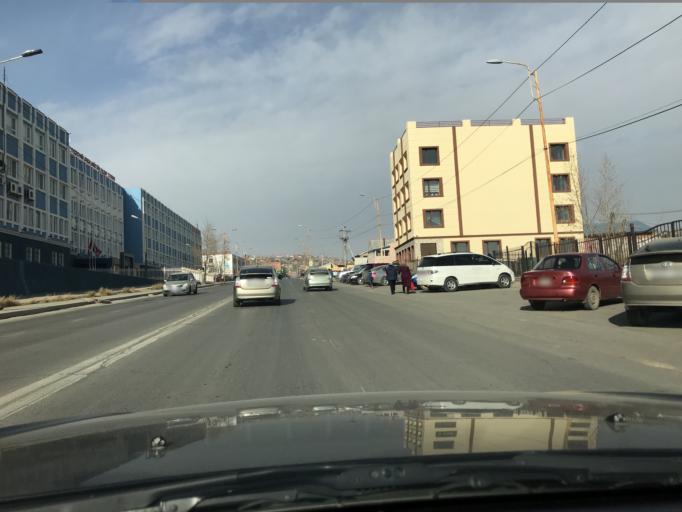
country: MN
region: Ulaanbaatar
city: Ulaanbaatar
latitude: 47.9289
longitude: 106.8908
